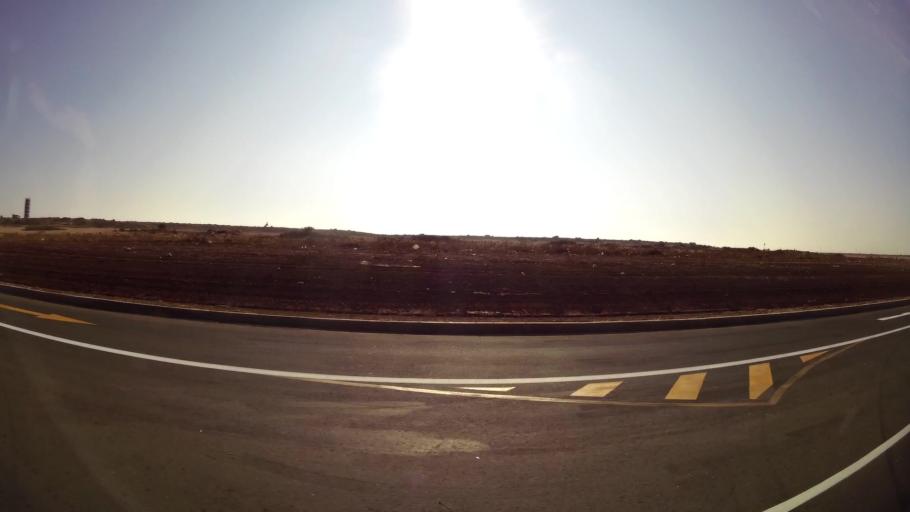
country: ZA
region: Orange Free State
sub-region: Mangaung Metropolitan Municipality
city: Bloemfontein
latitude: -29.1857
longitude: 26.2030
